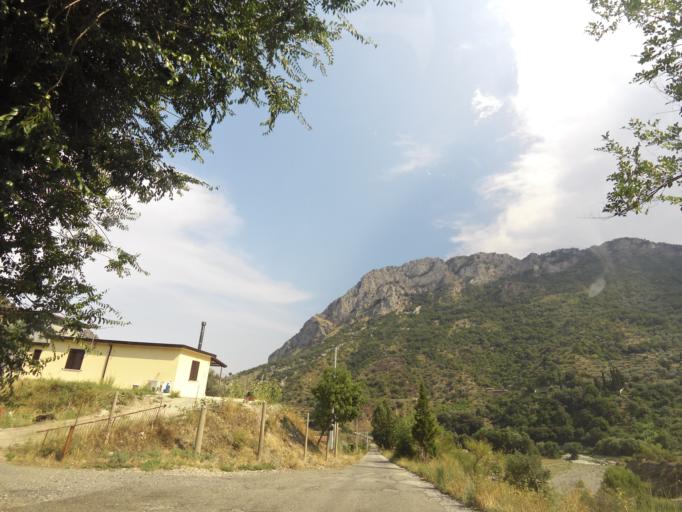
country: IT
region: Calabria
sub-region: Provincia di Reggio Calabria
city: Bivongi
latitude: 38.4892
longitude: 16.4579
